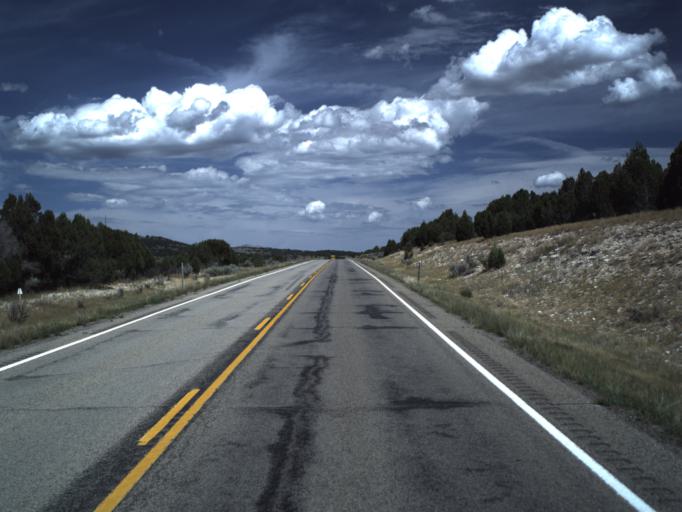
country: US
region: Utah
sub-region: Sanpete County
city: Fairview
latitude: 39.6631
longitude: -111.4522
